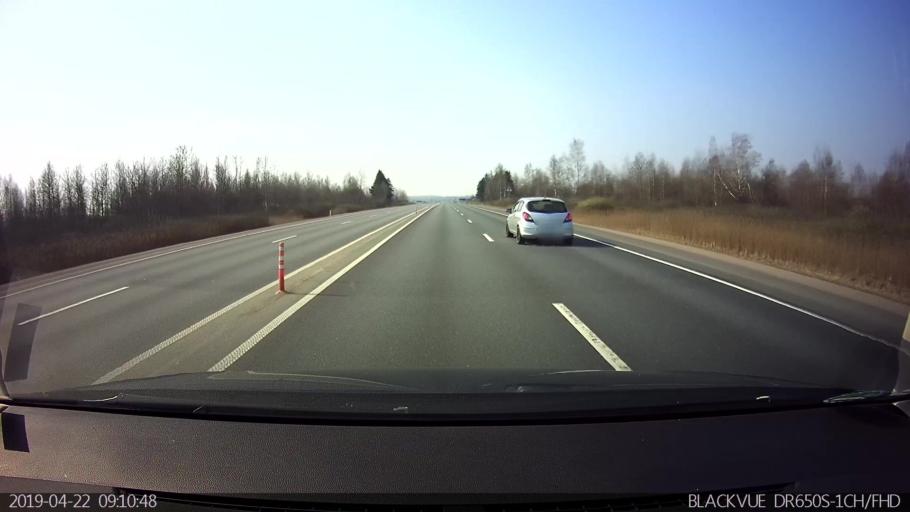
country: RU
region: Smolensk
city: Katyn'
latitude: 54.8352
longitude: 31.6603
